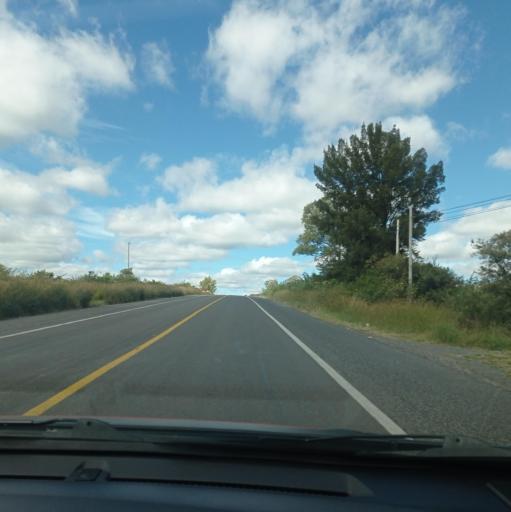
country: MX
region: Jalisco
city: San Diego de Alejandria
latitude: 20.9979
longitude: -101.9984
